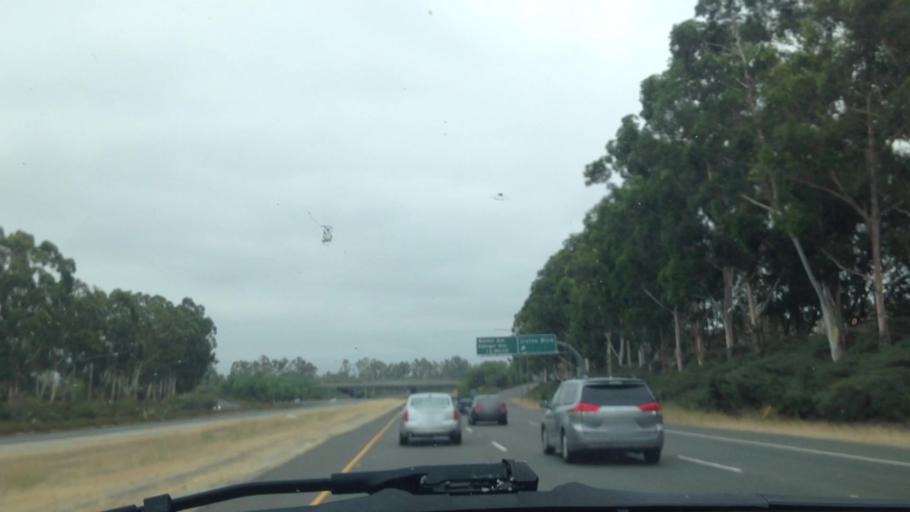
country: US
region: California
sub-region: Orange County
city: North Tustin
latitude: 33.7303
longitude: -117.7755
